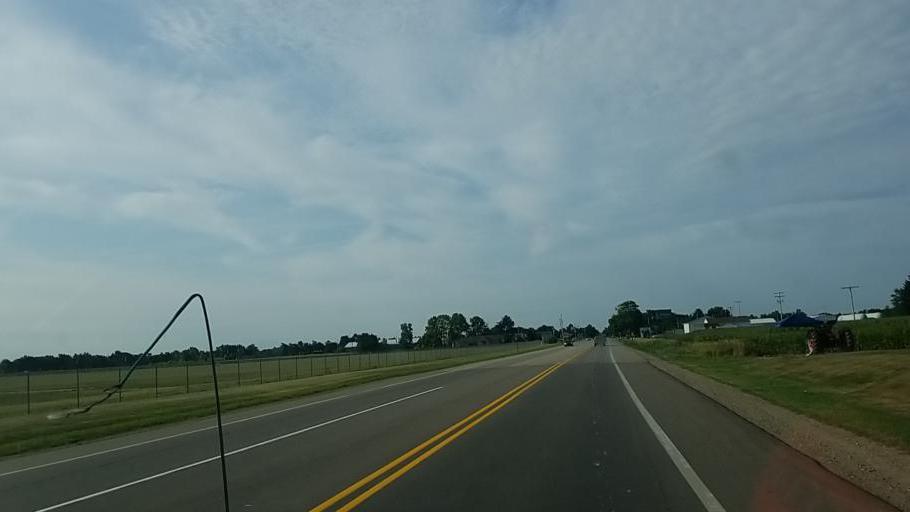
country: US
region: Michigan
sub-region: Ionia County
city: Ionia
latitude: 42.9396
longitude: -85.0748
